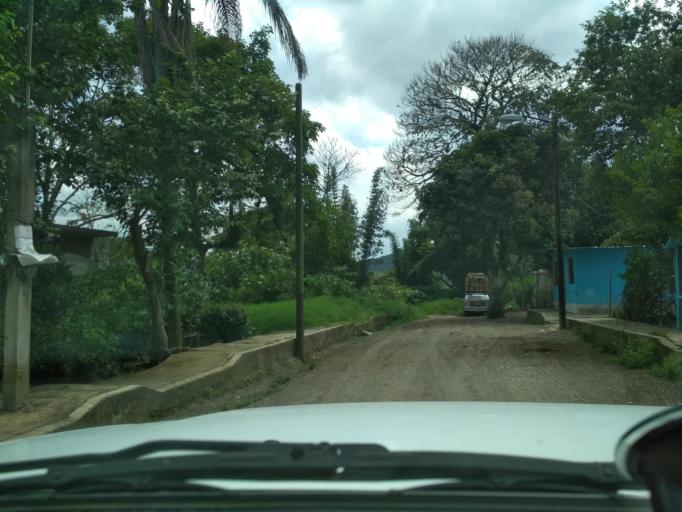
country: MX
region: Veracruz
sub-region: Fortin
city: Monte Salas
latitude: 18.9360
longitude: -97.0195
